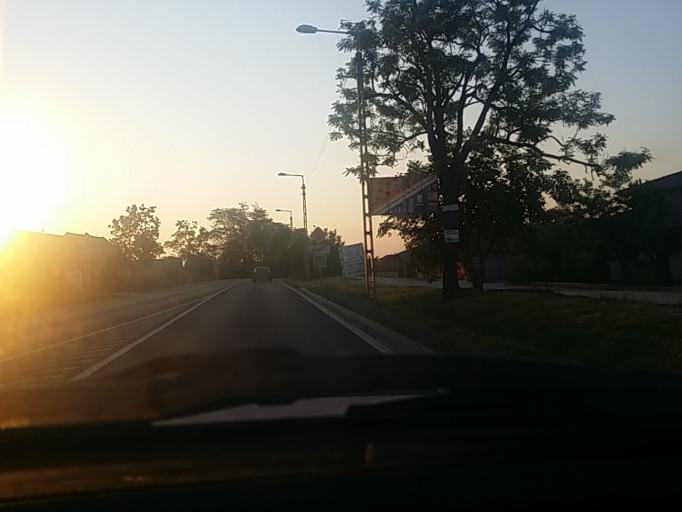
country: HU
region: Pest
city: Maglod
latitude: 47.4477
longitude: 19.3749
